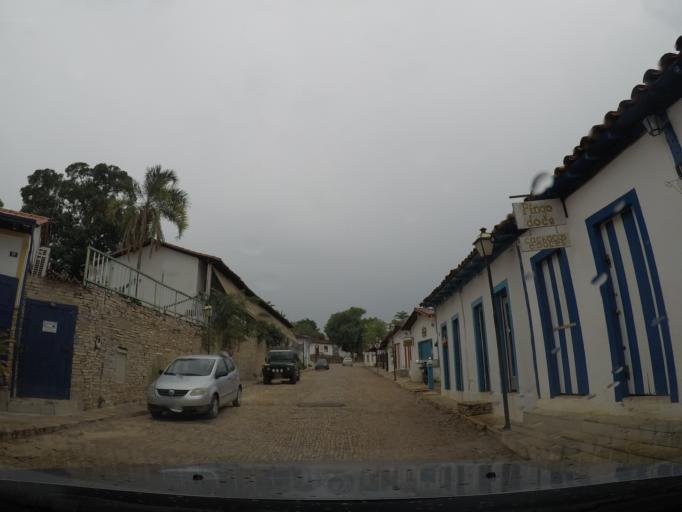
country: BR
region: Goias
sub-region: Pirenopolis
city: Pirenopolis
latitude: -15.8517
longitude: -48.9571
